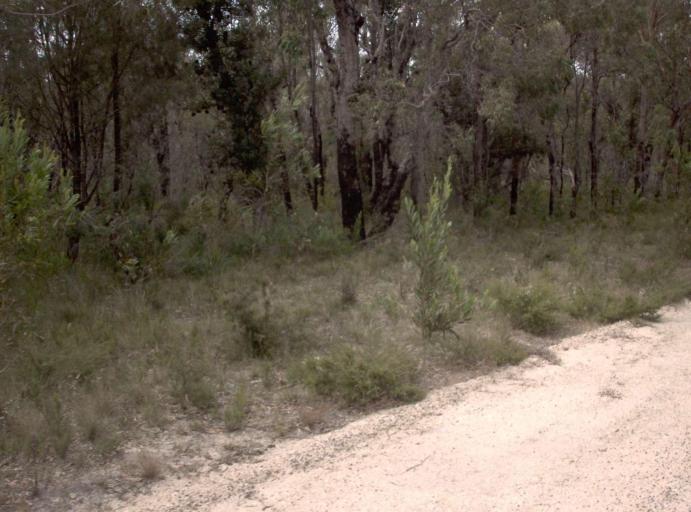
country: AU
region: New South Wales
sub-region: Bega Valley
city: Eden
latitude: -37.4213
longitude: 149.6485
